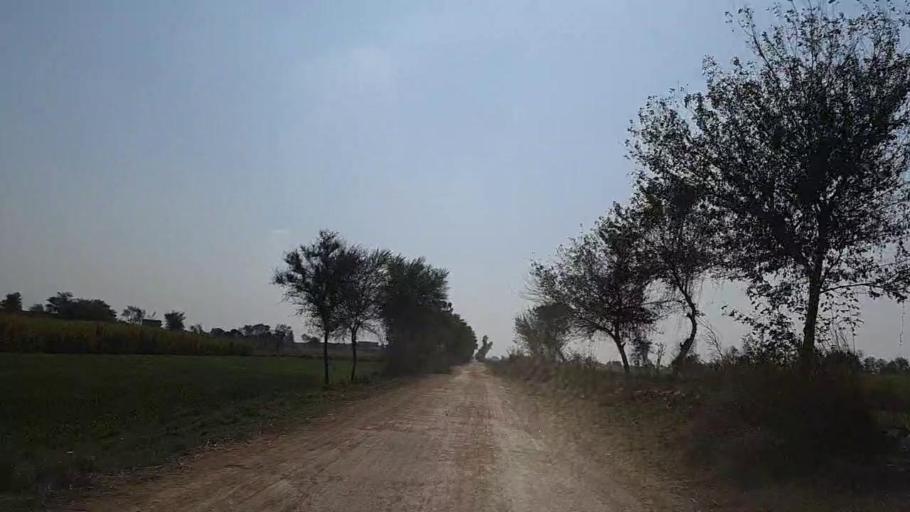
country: PK
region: Sindh
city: Daur
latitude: 26.4610
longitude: 68.2632
